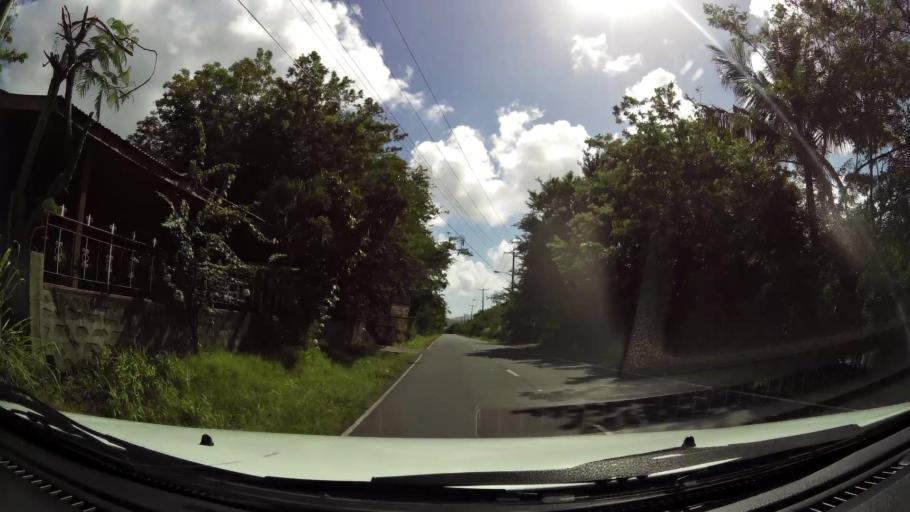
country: LC
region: Choiseul Quarter
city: Choiseul
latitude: 13.7582
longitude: -61.0179
